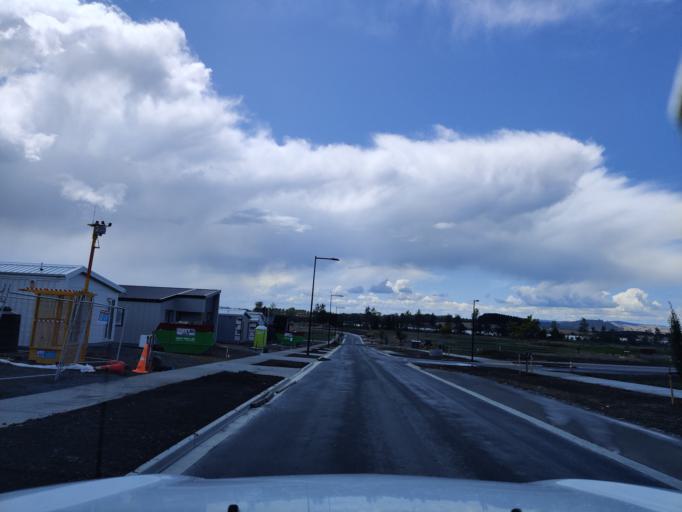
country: NZ
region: Waikato
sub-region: Waikato District
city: Te Kauwhata
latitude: -37.4128
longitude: 175.1505
